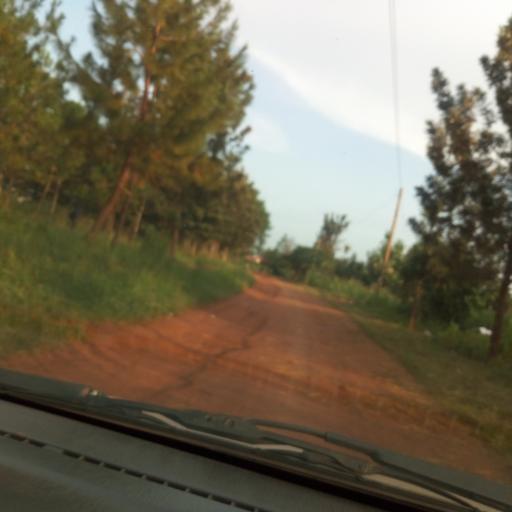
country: UG
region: Western Region
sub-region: Kiryandongo District
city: Kiryandongo
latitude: 1.8061
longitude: 32.0046
